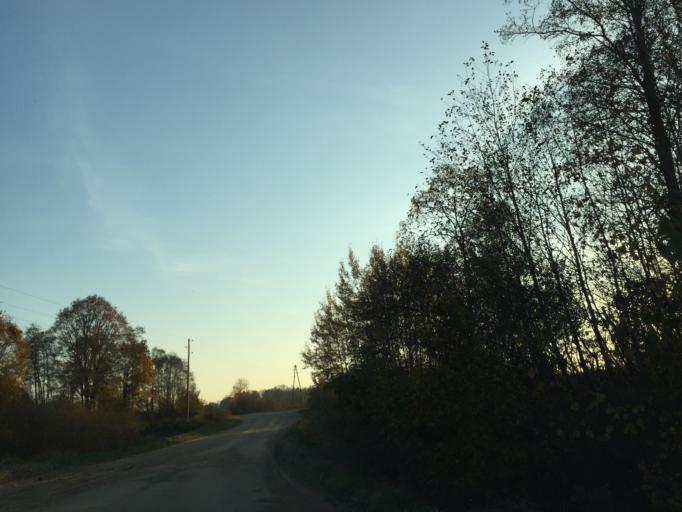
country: LV
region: Vainode
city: Vainode
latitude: 56.5086
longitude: 21.8249
